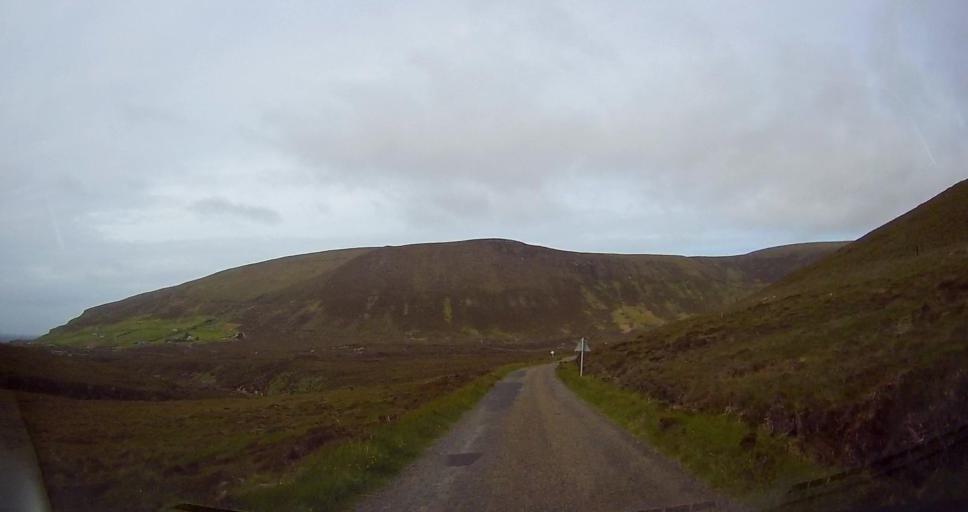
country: GB
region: Scotland
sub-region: Orkney Islands
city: Stromness
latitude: 58.8817
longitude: -3.3727
